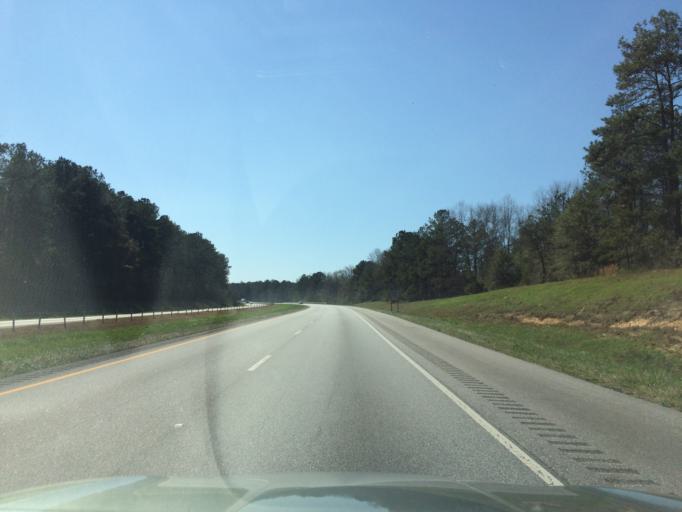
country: US
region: Alabama
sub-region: Macon County
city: Tuskegee
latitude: 32.4675
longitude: -85.7102
